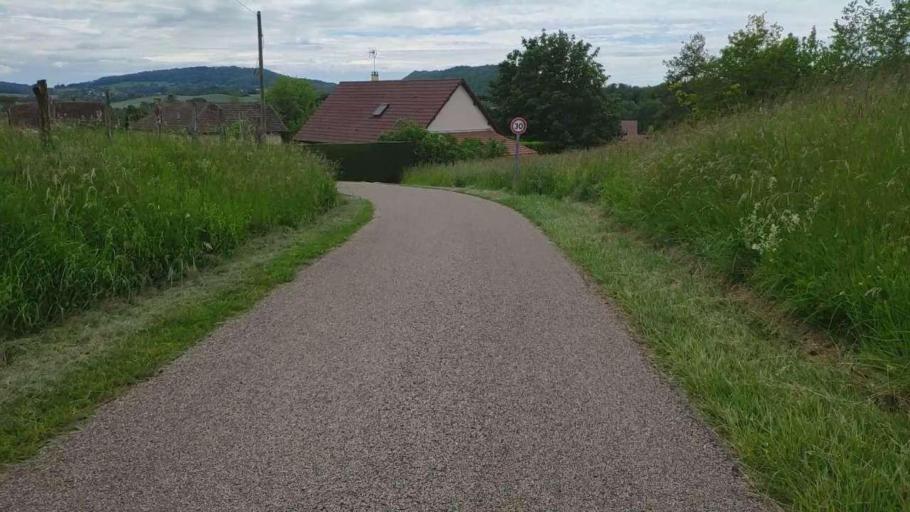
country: FR
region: Franche-Comte
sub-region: Departement du Jura
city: Lons-le-Saunier
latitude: 46.7527
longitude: 5.5639
